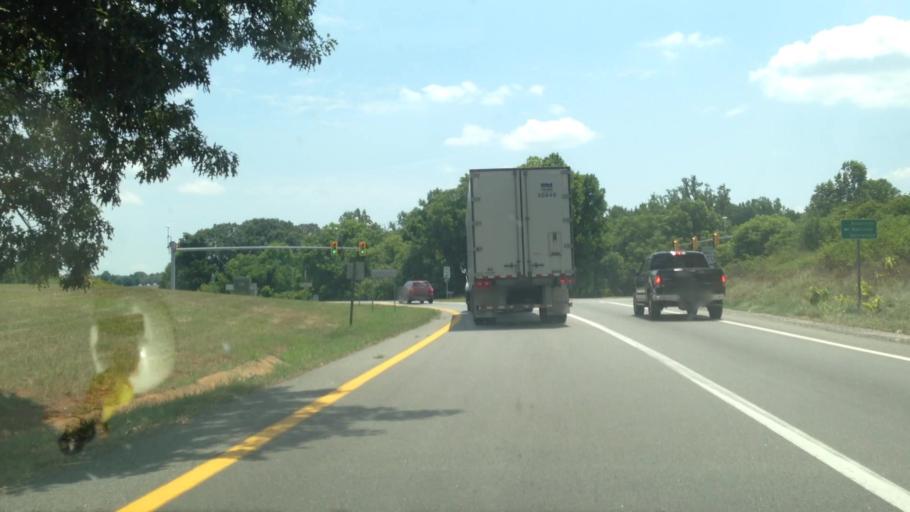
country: US
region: Virginia
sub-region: Henry County
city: Chatmoss
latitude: 36.6222
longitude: -79.8611
